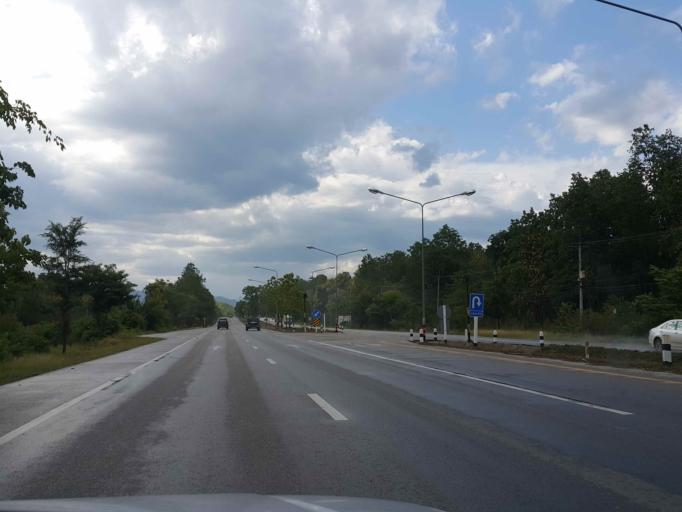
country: TH
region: Lampang
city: Thoen
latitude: 17.6759
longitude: 99.2428
